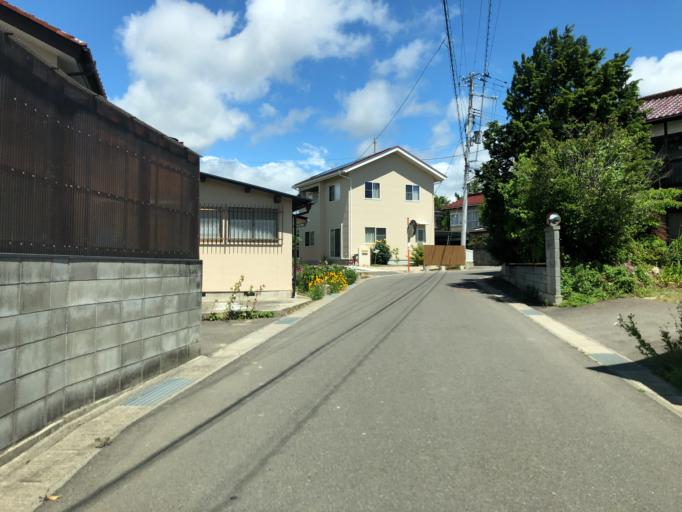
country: JP
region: Fukushima
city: Fukushima-shi
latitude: 37.8027
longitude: 140.4359
